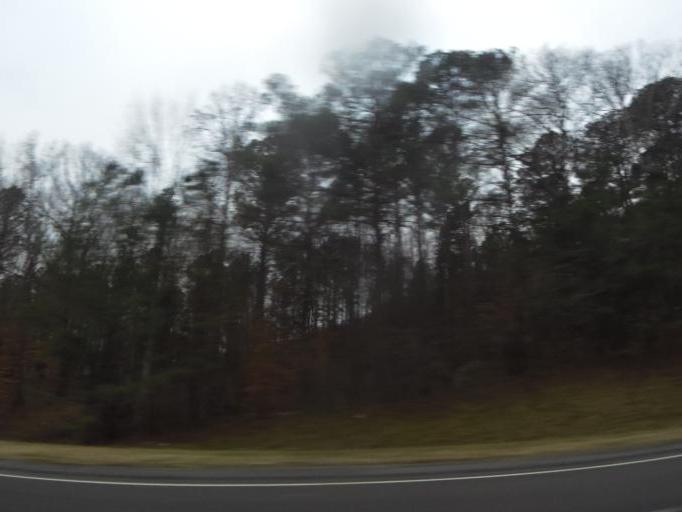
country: US
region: Alabama
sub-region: Blount County
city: Smoke Rise
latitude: 33.8902
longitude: -86.8515
